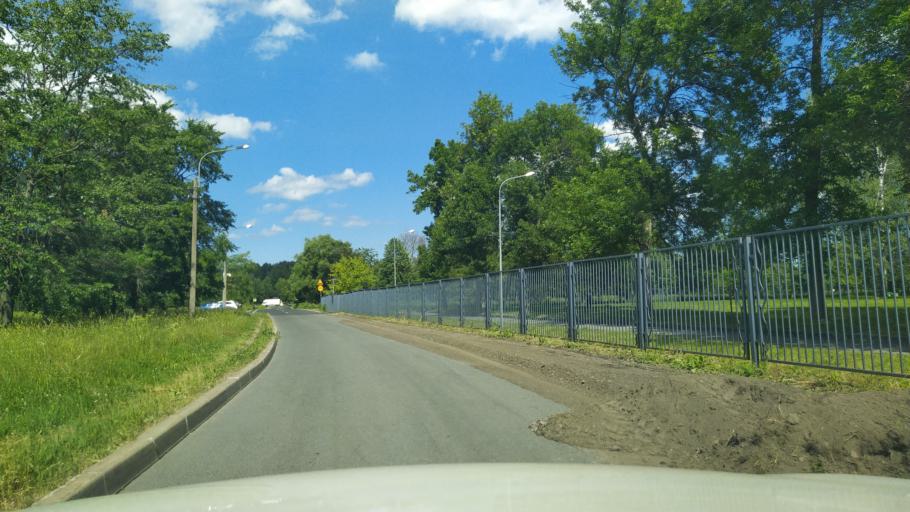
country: RU
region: Leningrad
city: Akademicheskoe
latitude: 59.9988
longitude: 30.4184
